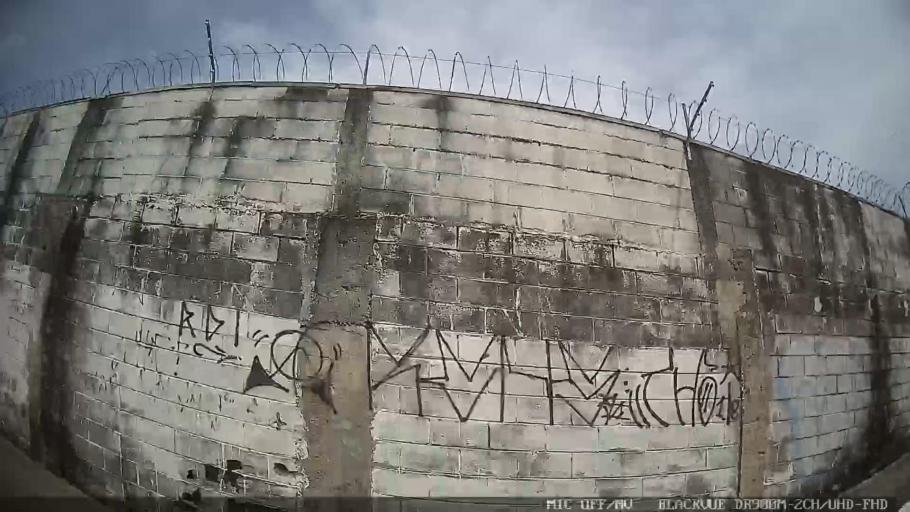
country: BR
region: Sao Paulo
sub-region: Ferraz De Vasconcelos
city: Ferraz de Vasconcelos
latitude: -23.5472
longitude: -46.3779
